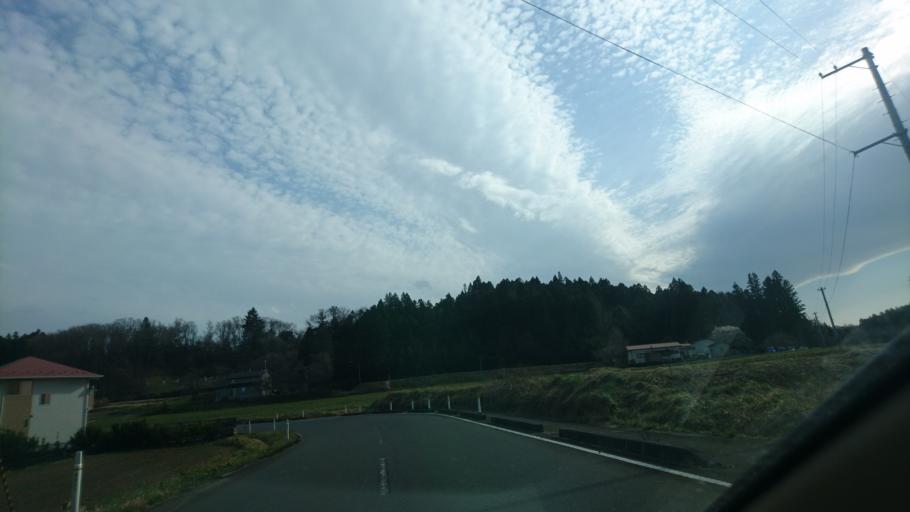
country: JP
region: Iwate
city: Ichinoseki
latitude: 38.8119
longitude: 141.0268
